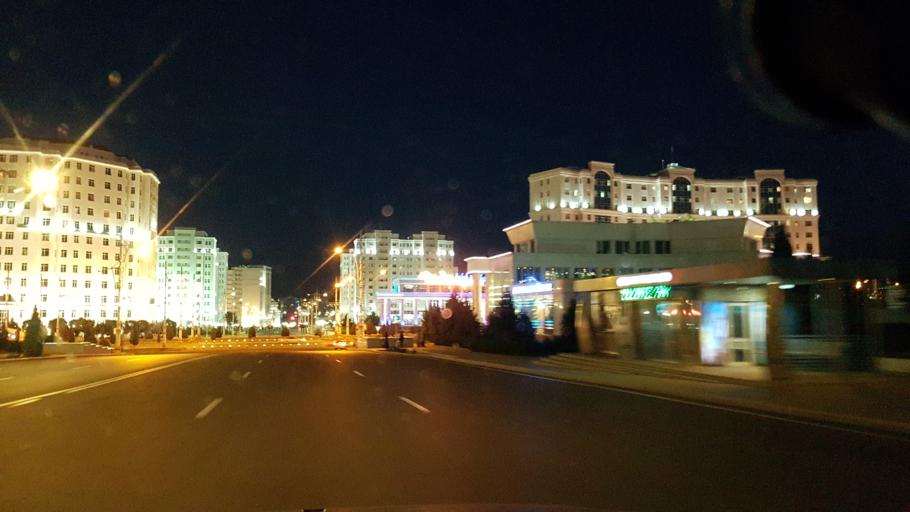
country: TM
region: Ahal
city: Ashgabat
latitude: 37.9203
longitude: 58.3515
